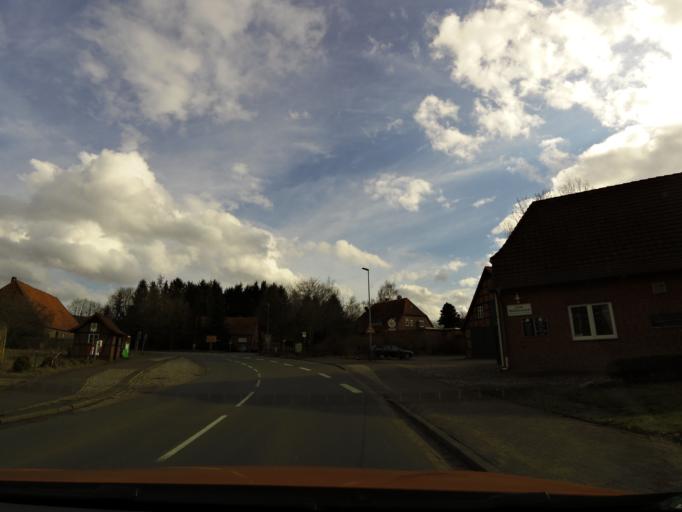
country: DE
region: Lower Saxony
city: Sudwalde
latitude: 52.8398
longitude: 8.8445
